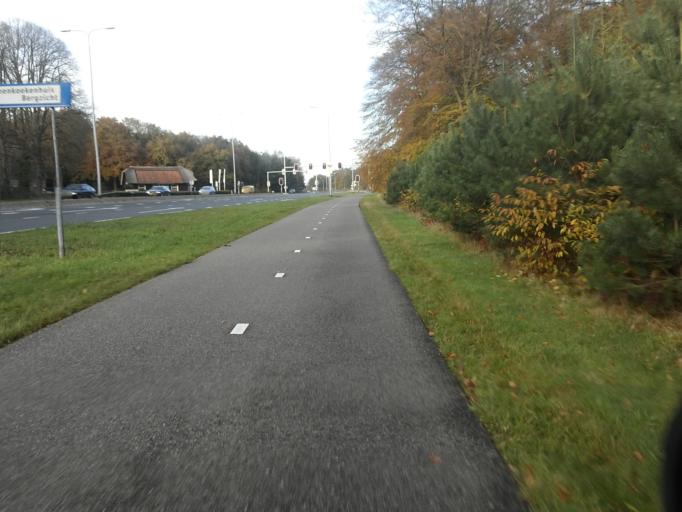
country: NL
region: Utrecht
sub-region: Gemeente Utrechtse Heuvelrug
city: Maarn
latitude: 52.0907
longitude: 5.3618
